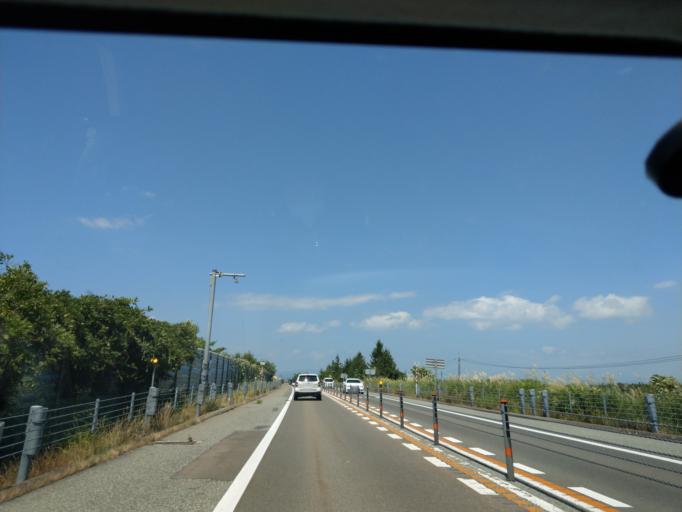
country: JP
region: Akita
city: Omagari
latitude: 39.3896
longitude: 140.4788
